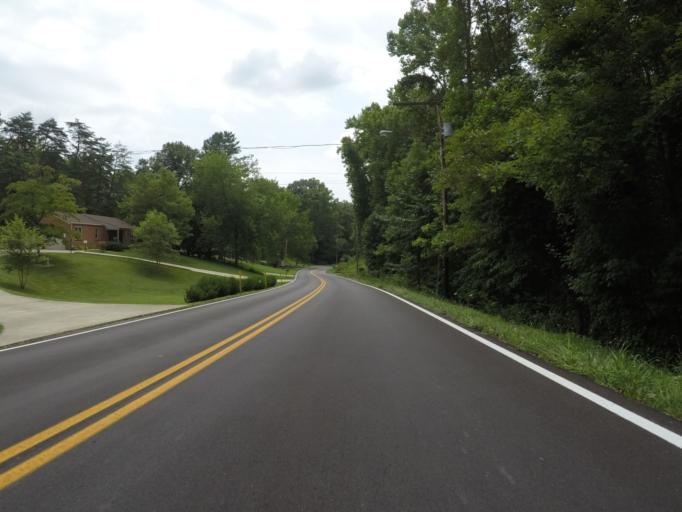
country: US
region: Kentucky
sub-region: Boyd County
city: Ashland
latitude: 38.4479
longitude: -82.6373
